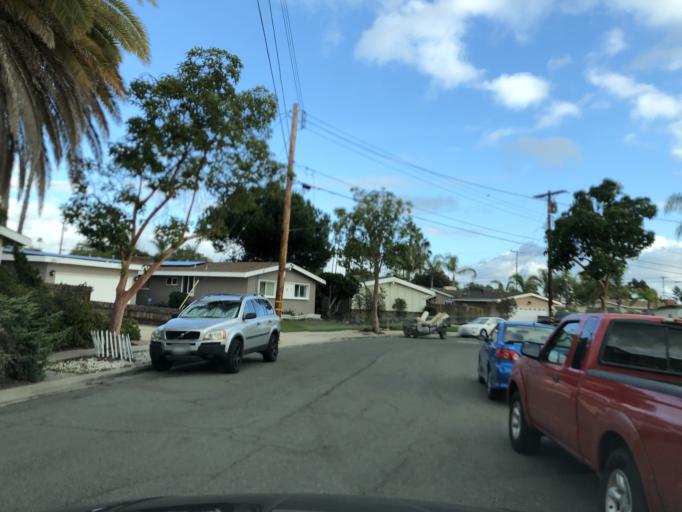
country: US
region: California
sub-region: San Diego County
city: La Jolla
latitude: 32.8141
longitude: -117.1871
